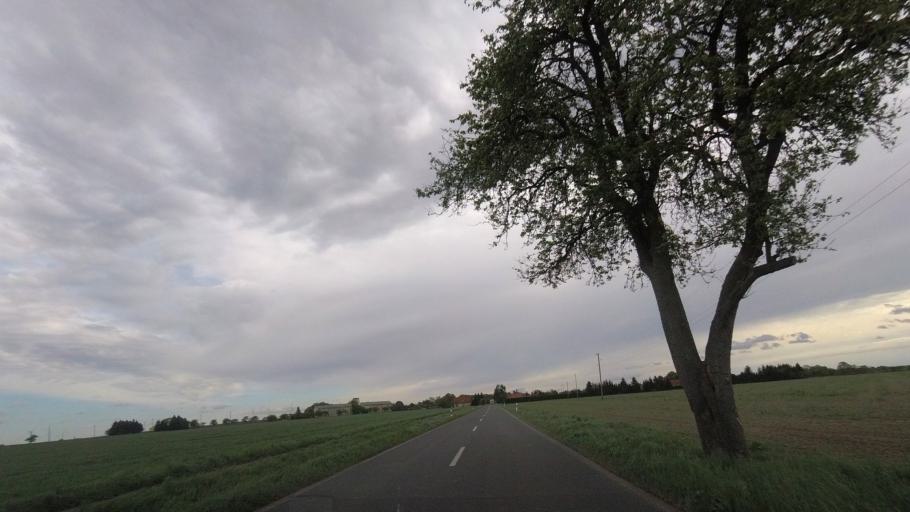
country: DE
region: Brandenburg
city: Ihlow
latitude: 51.9203
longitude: 13.3268
